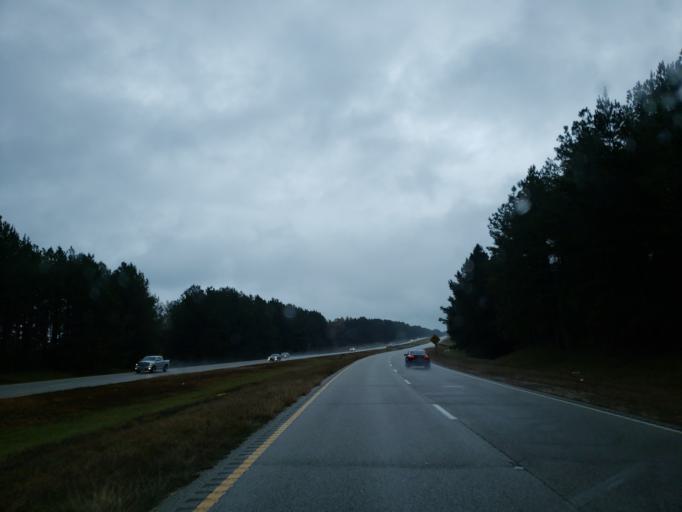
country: US
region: Mississippi
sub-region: Lauderdale County
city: Meridian
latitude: 32.2867
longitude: -88.6983
